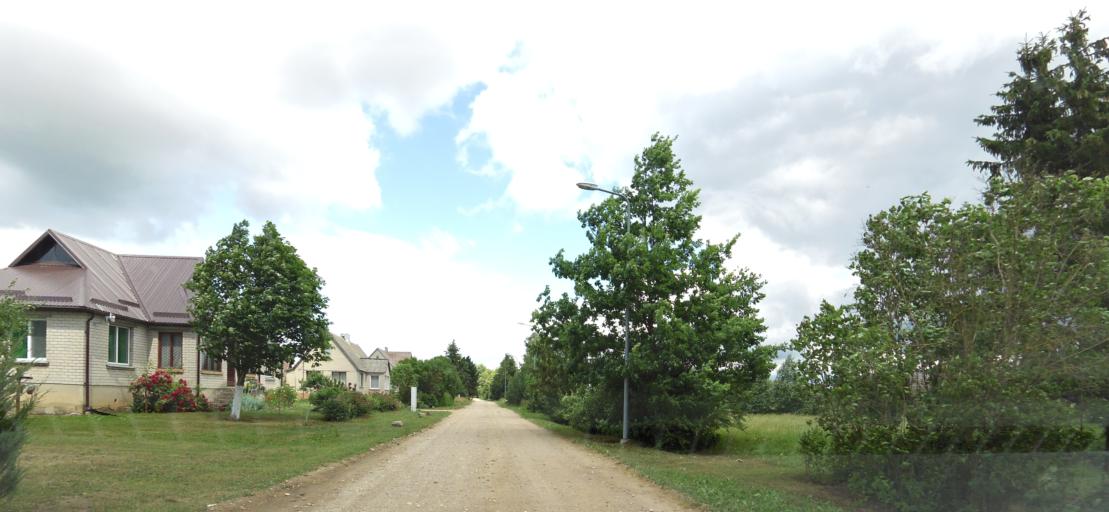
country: LT
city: Kupiskis
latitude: 55.8396
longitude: 24.9351
